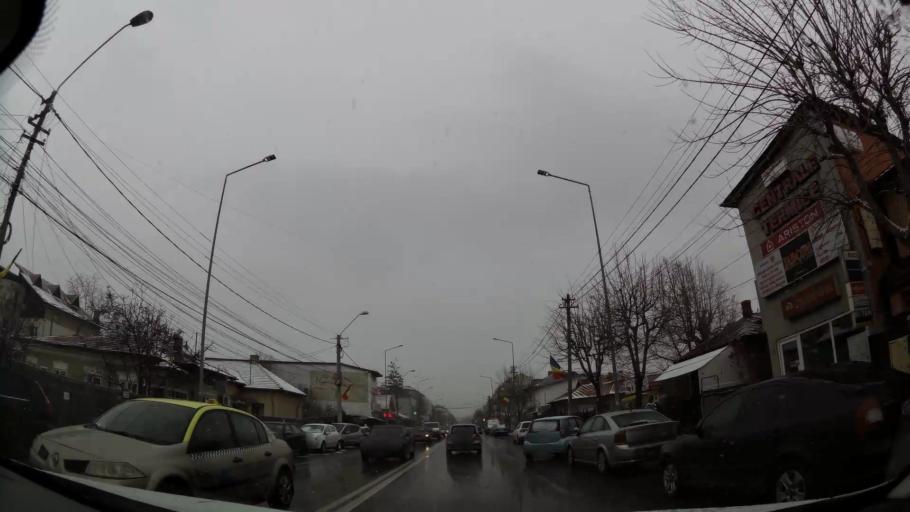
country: RO
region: Dambovita
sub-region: Municipiul Targoviste
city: Targoviste
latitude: 44.9229
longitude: 25.4524
